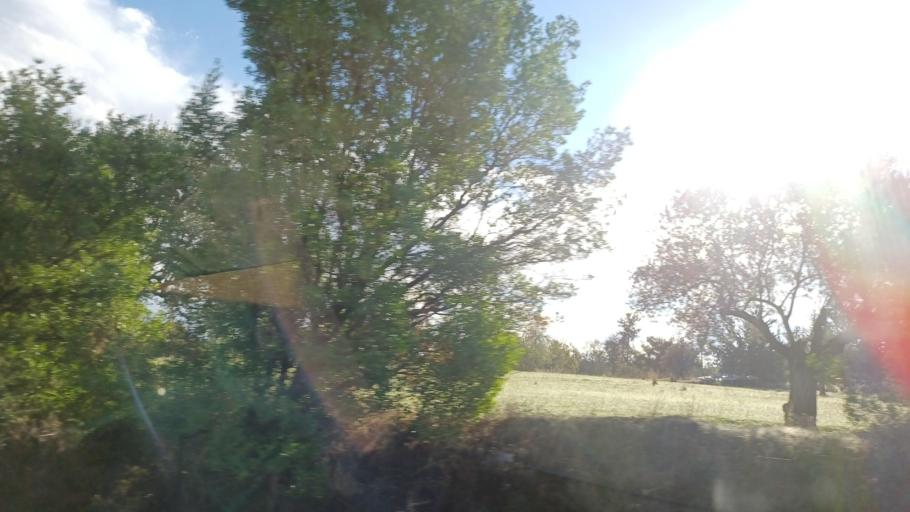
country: CY
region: Lefkosia
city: Lythrodontas
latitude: 34.9521
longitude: 33.3225
